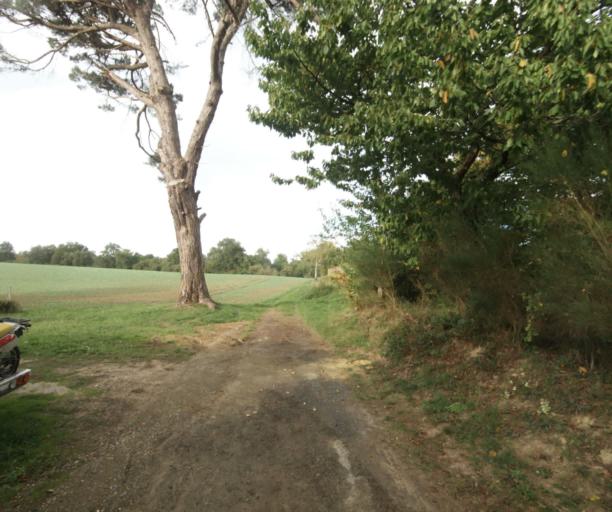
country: FR
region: Midi-Pyrenees
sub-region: Departement du Gers
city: Le Houga
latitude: 43.8585
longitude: -0.1427
